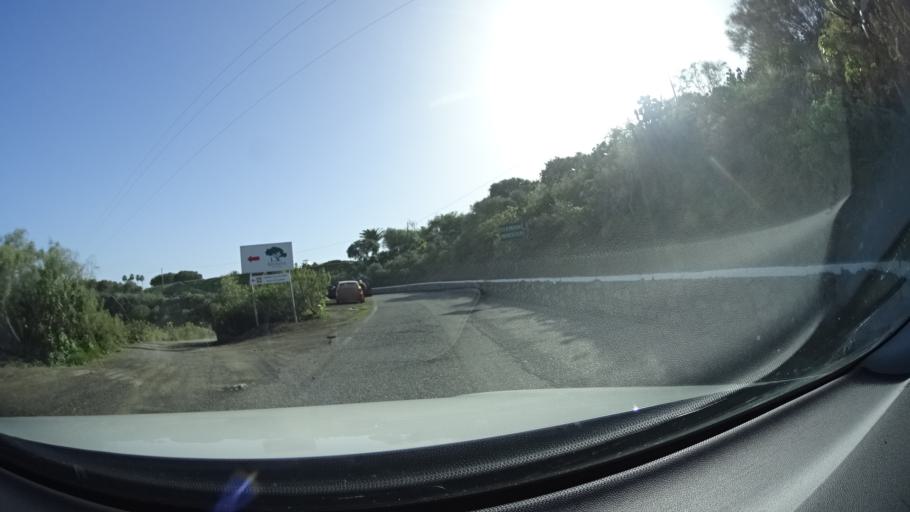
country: ES
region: Canary Islands
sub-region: Provincia de Las Palmas
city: Santa Brigida
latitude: 28.0337
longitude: -15.4611
